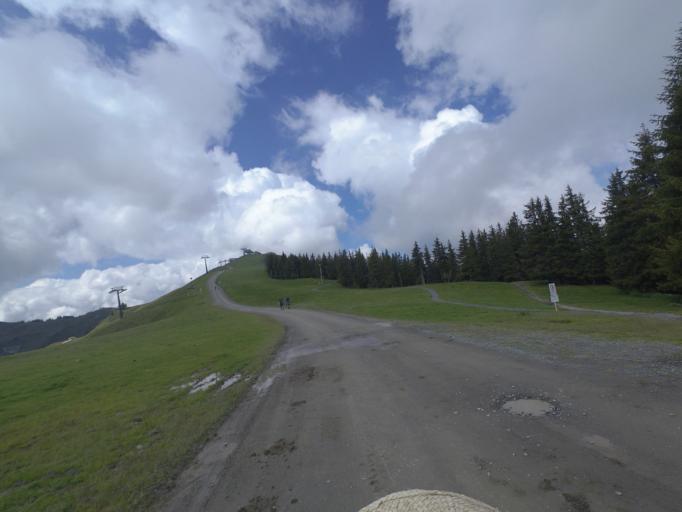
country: AT
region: Salzburg
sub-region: Politischer Bezirk Zell am See
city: Viehhofen
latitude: 47.4093
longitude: 12.7116
